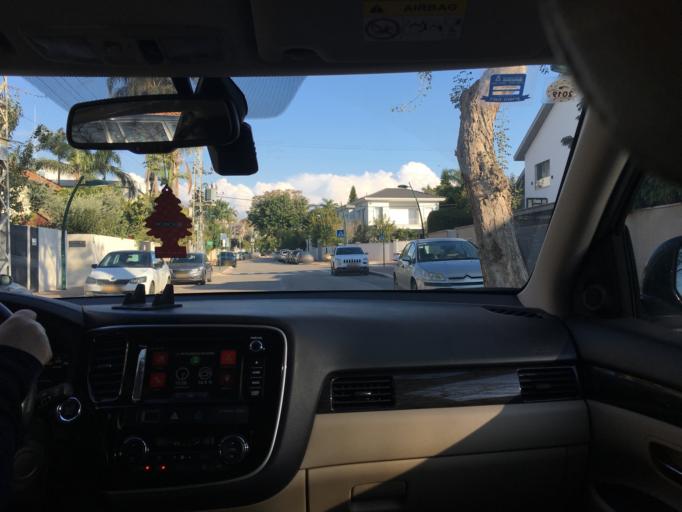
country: IL
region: Tel Aviv
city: Ramat HaSharon
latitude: 32.1511
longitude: 34.8309
